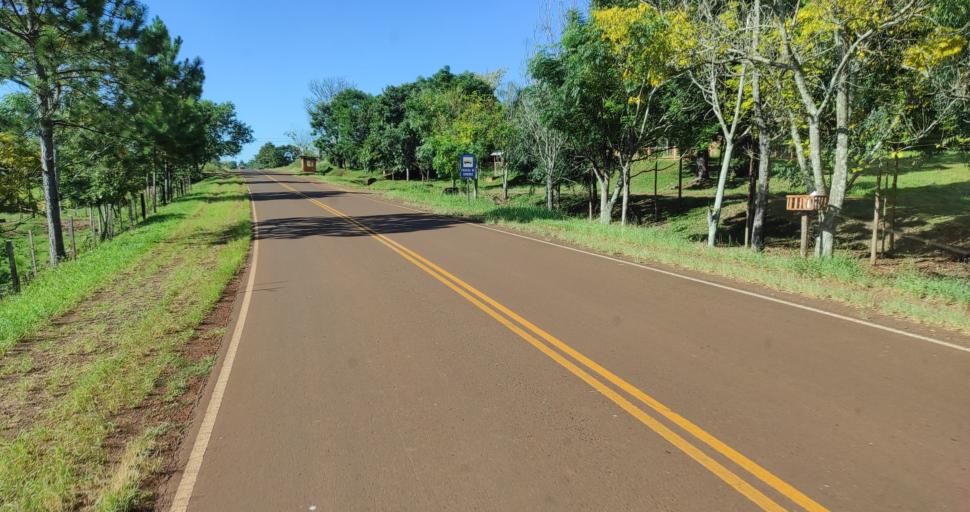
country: AR
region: Misiones
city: El Soberbio
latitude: -27.2298
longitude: -54.1785
